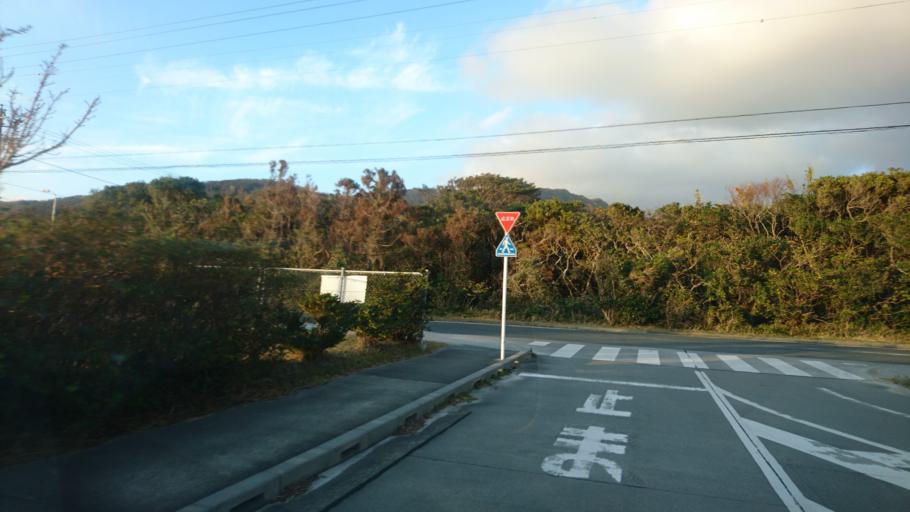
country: JP
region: Shizuoka
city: Shimoda
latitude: 34.3708
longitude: 139.2691
